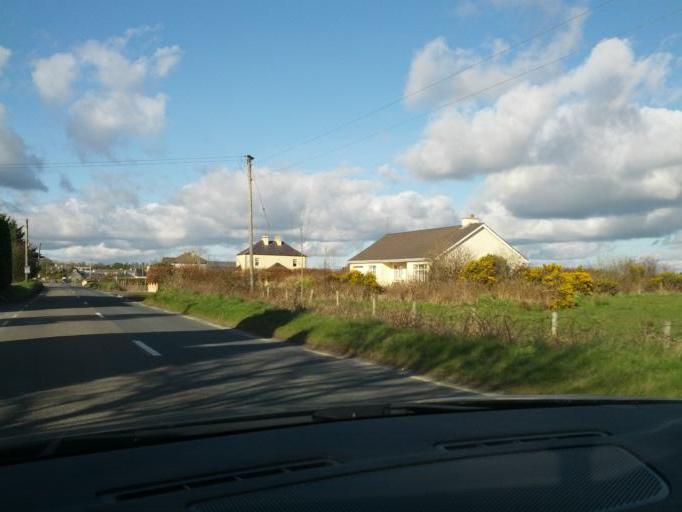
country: IE
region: Connaught
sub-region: Roscommon
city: Castlerea
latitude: 53.5974
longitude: -8.5635
